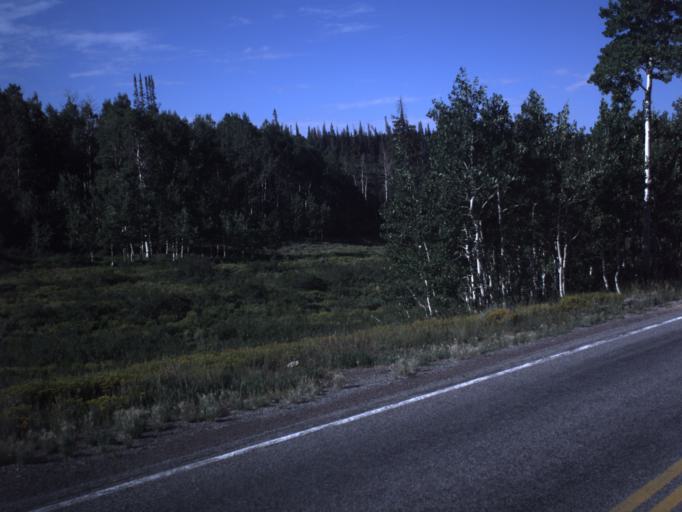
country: US
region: Utah
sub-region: Sanpete County
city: Fairview
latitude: 39.6783
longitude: -111.3182
